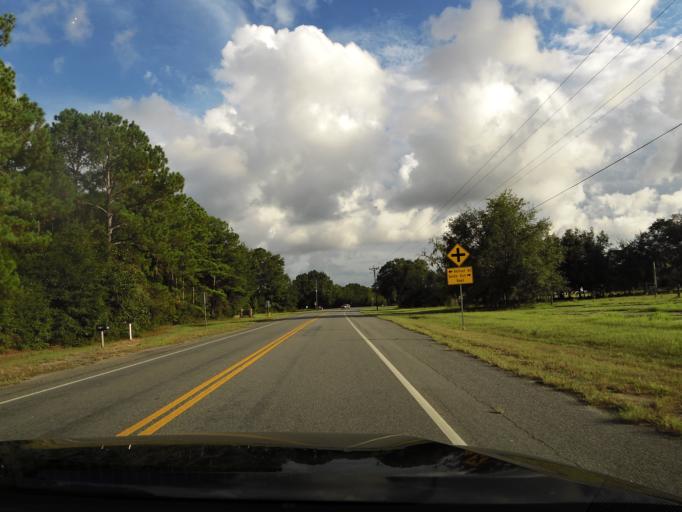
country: US
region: Georgia
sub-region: Liberty County
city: Midway
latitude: 31.7043
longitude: -81.4148
